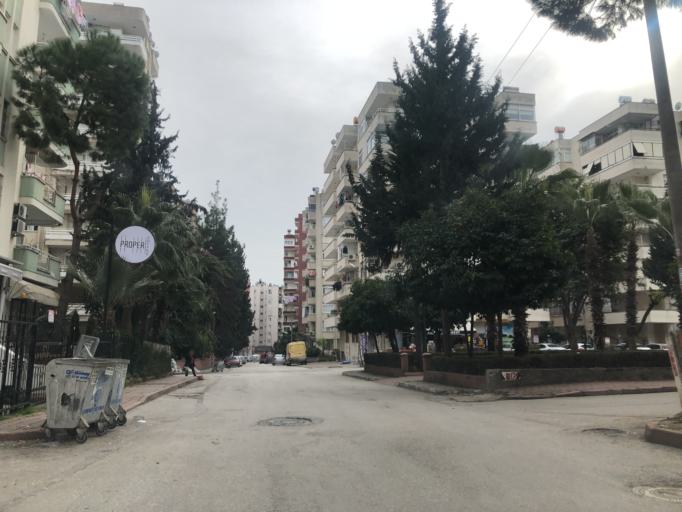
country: TR
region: Adana
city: Adana
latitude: 37.0510
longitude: 35.2928
